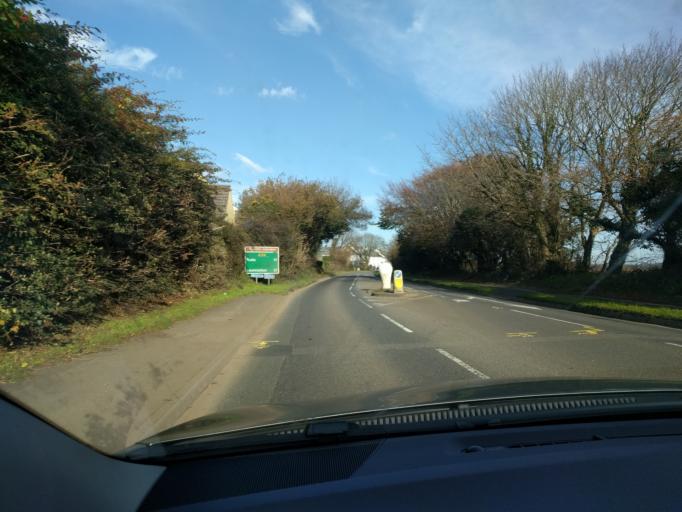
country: GB
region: England
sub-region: Cornwall
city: Camelford
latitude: 50.6139
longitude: -4.6859
